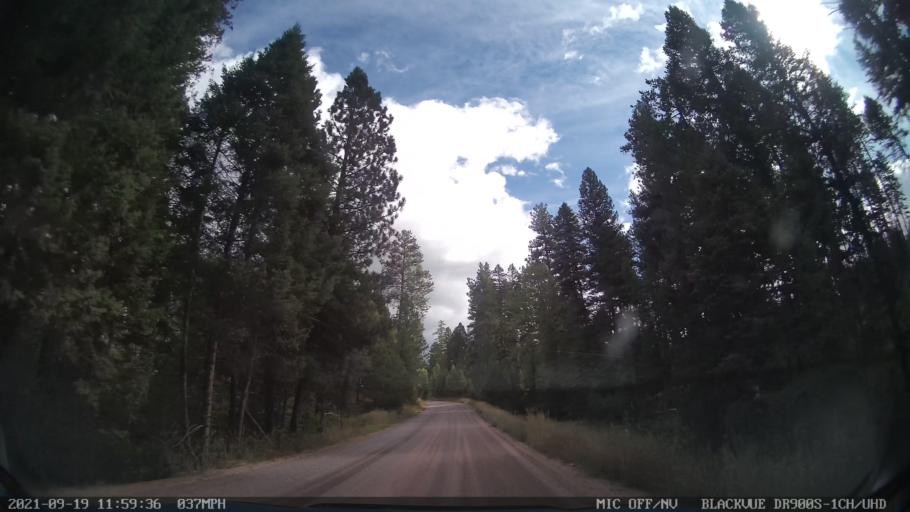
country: US
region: Montana
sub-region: Missoula County
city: Seeley Lake
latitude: 47.1861
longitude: -113.4758
